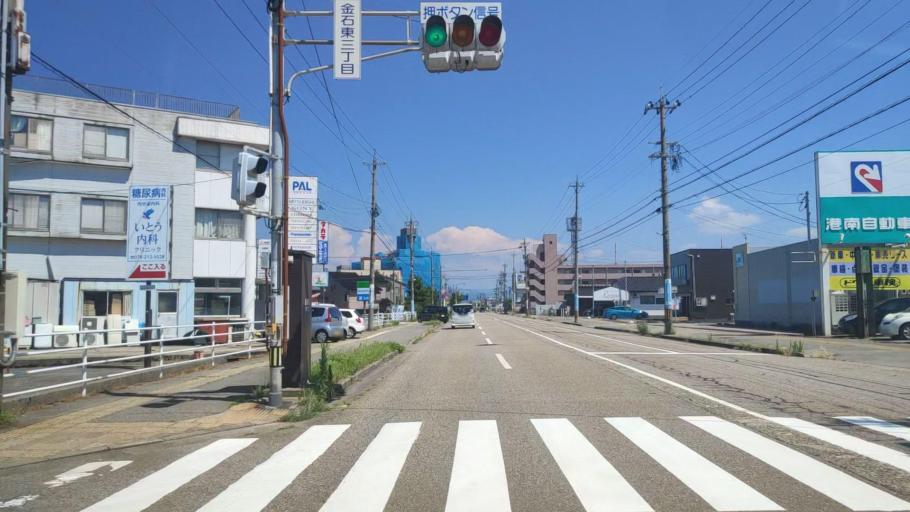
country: JP
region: Ishikawa
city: Kanazawa-shi
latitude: 36.6006
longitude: 136.5949
